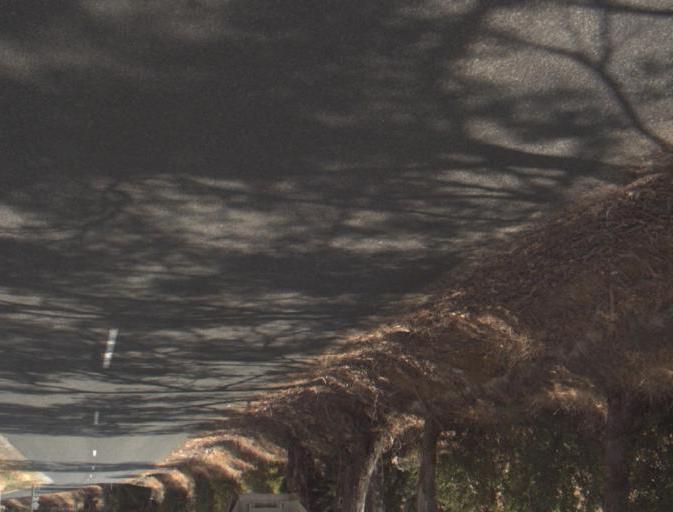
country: AU
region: Tasmania
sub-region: Launceston
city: Newstead
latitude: -41.4764
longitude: 147.1885
